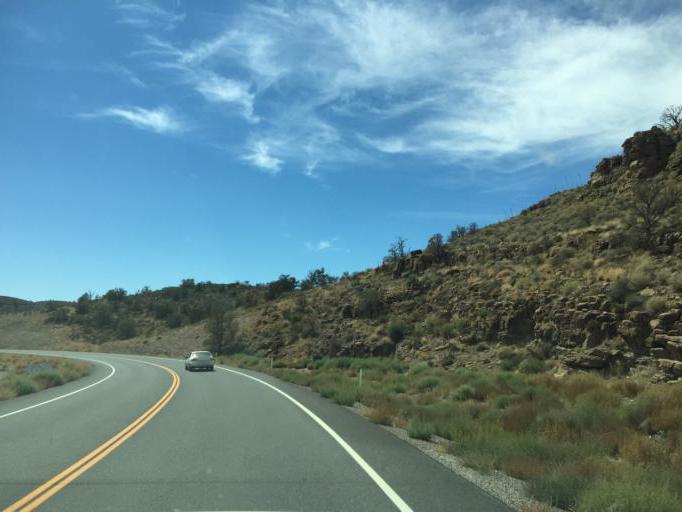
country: US
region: Arizona
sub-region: Mohave County
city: Meadview
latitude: 35.9115
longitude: -113.9289
